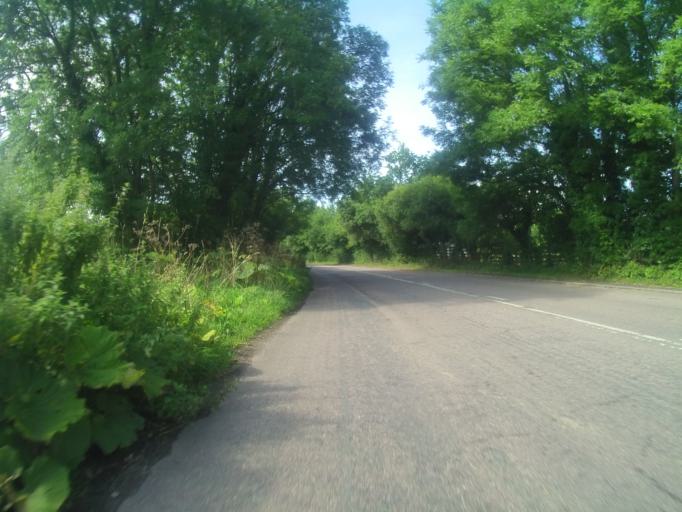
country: GB
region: England
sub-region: Devon
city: Ashburton
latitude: 50.5080
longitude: -3.7674
